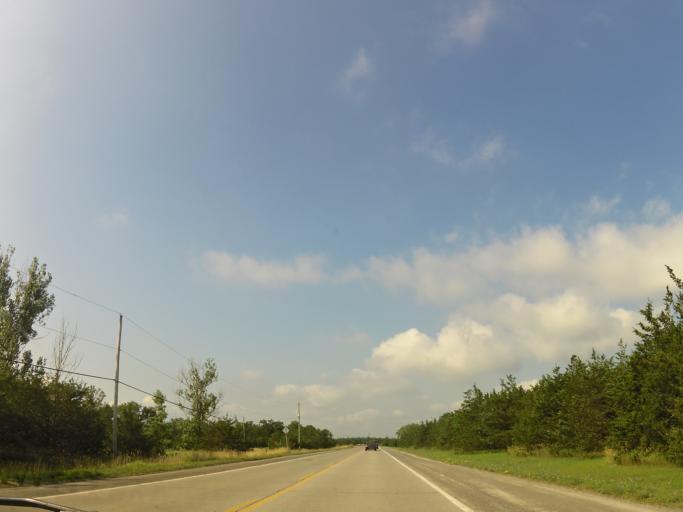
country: CA
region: Ontario
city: Picton
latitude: 44.0894
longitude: -77.0875
